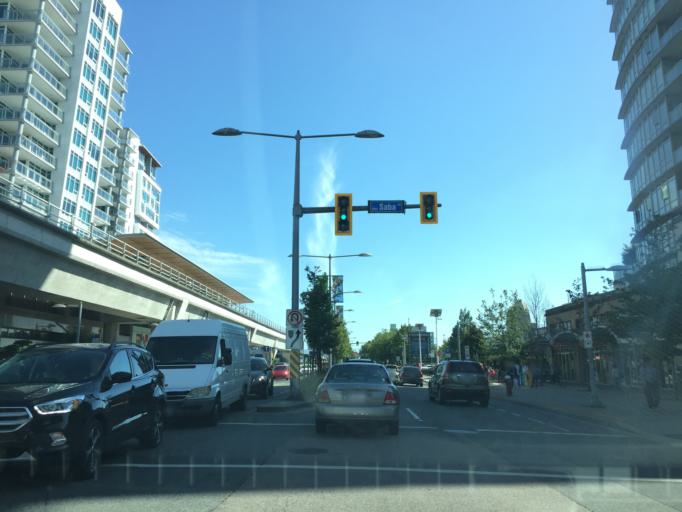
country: CA
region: British Columbia
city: Richmond
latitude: 49.1689
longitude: -123.1366
